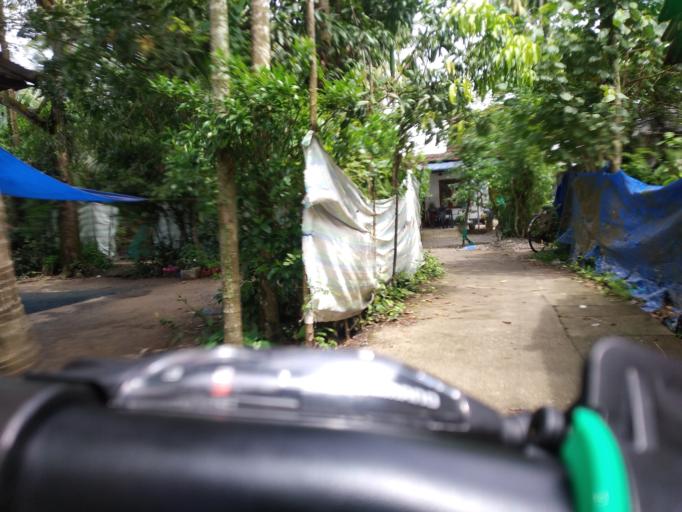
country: IN
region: Kerala
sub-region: Ernakulam
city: Elur
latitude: 10.0771
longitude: 76.2151
